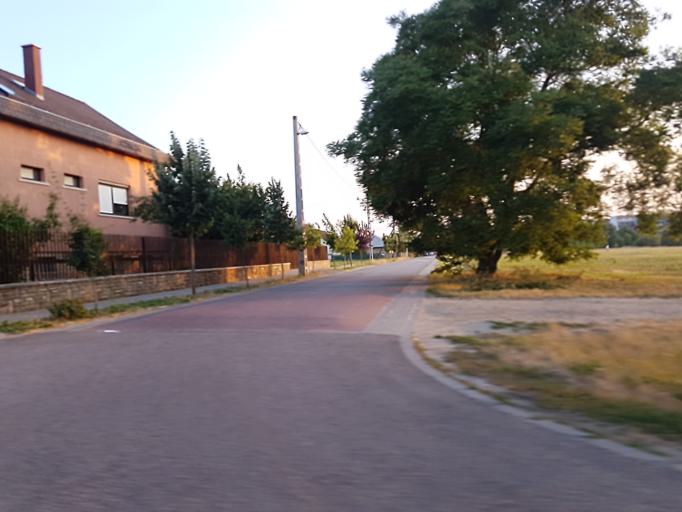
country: HU
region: Budapest
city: Budapest XVI. keruelet
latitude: 47.5331
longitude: 19.1625
